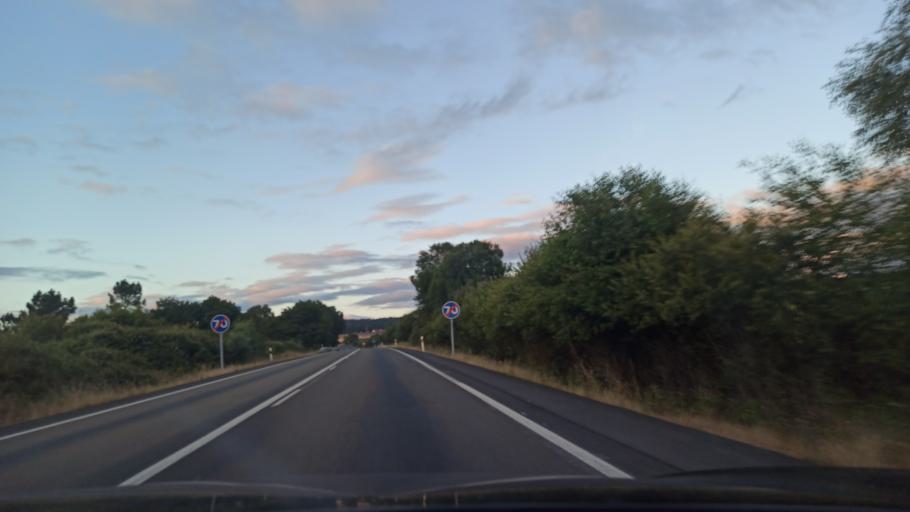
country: ES
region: Galicia
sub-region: Provincia de Lugo
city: Monterroso
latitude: 42.8072
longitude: -7.7786
